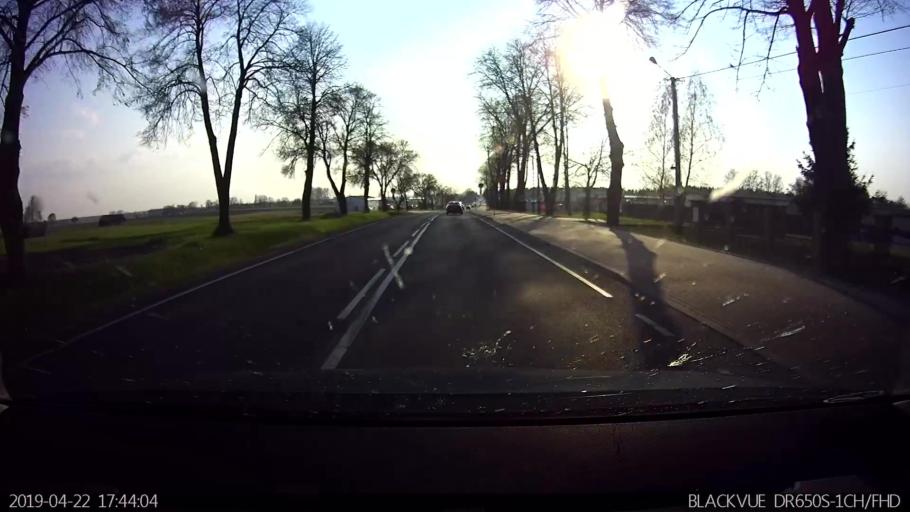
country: PL
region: Masovian Voivodeship
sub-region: Powiat wegrowski
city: Wegrow
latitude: 52.4032
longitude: 22.0540
